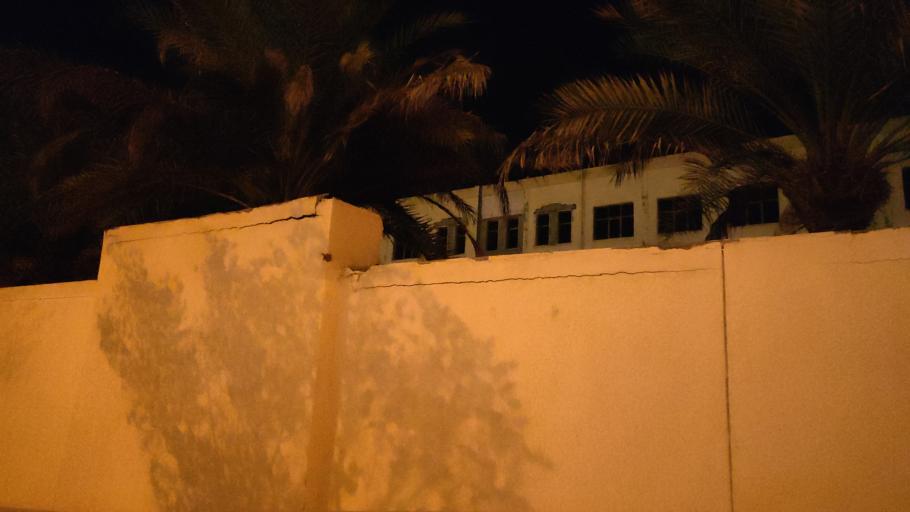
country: KW
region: Al Asimah
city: Ash Shamiyah
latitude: 29.3297
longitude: 47.9829
